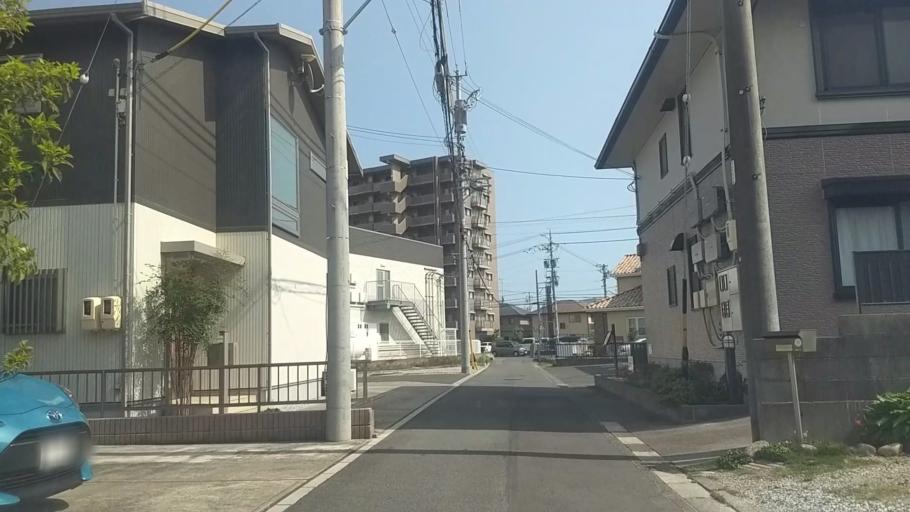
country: JP
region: Shizuoka
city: Hamamatsu
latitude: 34.7177
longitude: 137.7766
